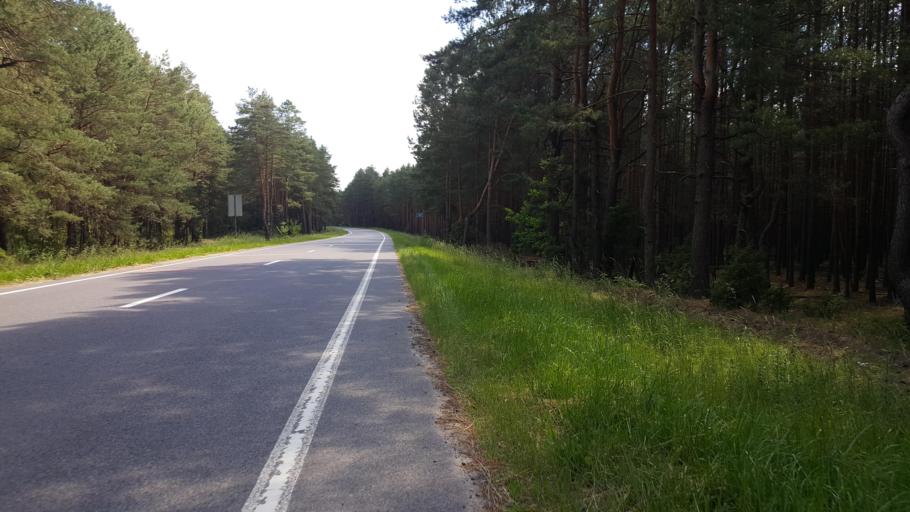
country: BY
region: Brest
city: Kamyanyuki
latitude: 52.5170
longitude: 23.6592
